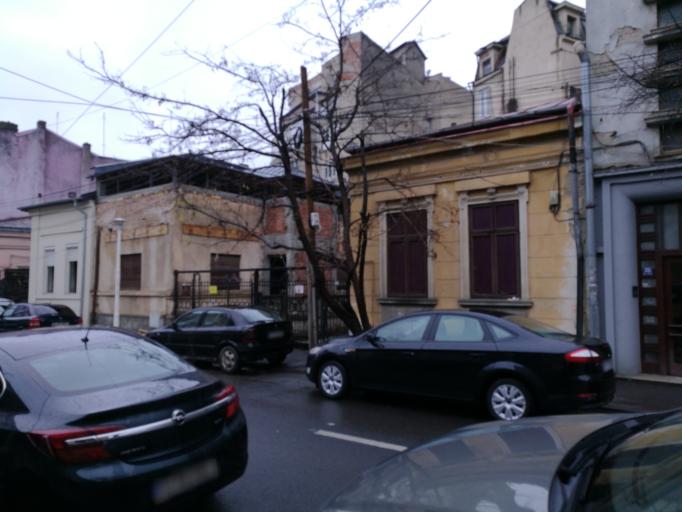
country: RO
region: Bucuresti
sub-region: Municipiul Bucuresti
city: Bucharest
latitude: 44.4375
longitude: 26.1165
